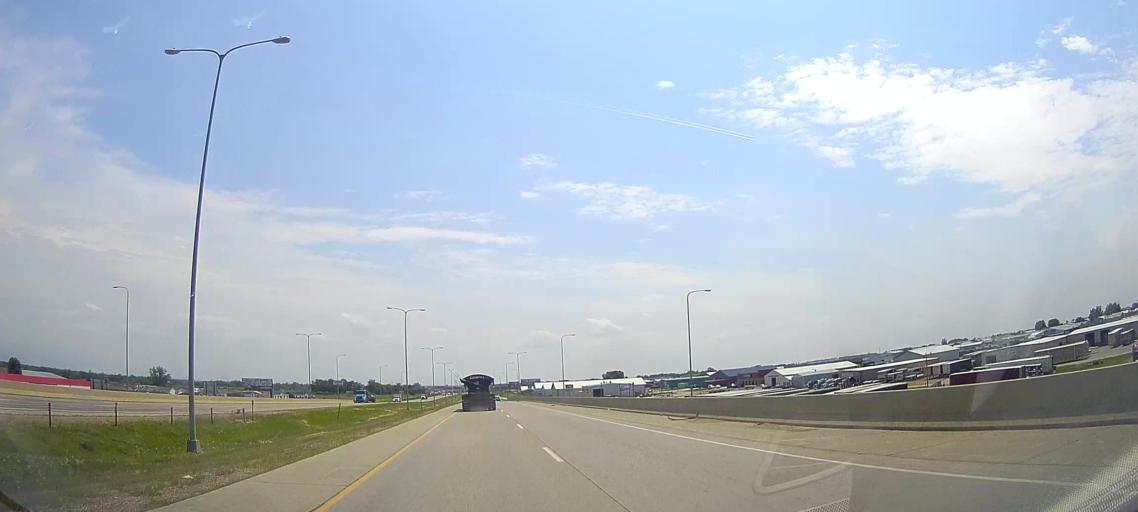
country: US
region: South Dakota
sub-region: Lincoln County
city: Tea
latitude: 43.4597
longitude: -96.7977
